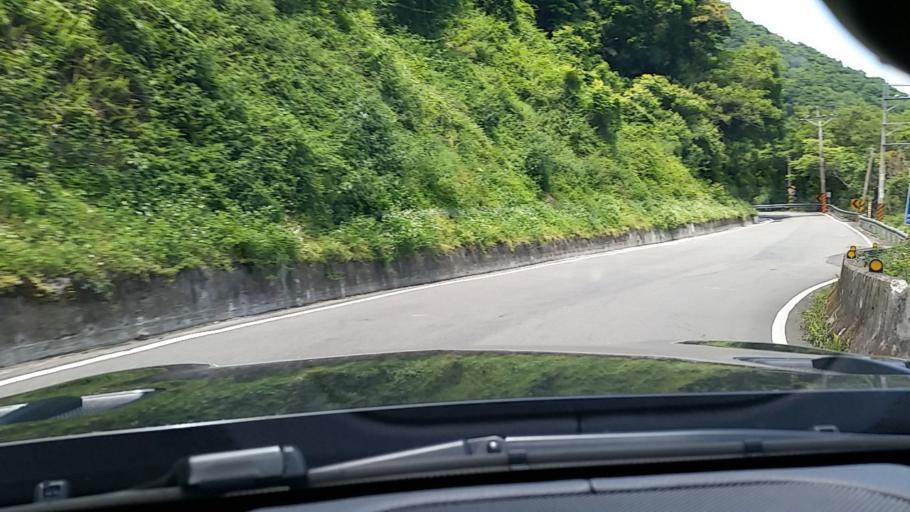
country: TW
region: Taiwan
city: Daxi
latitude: 24.6982
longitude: 121.3658
